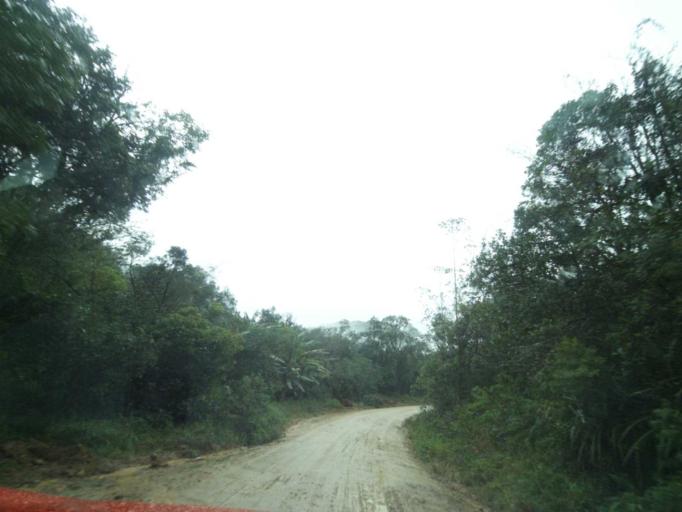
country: BR
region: Santa Catarina
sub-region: Anitapolis
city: Anitapolis
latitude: -27.9083
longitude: -49.1950
